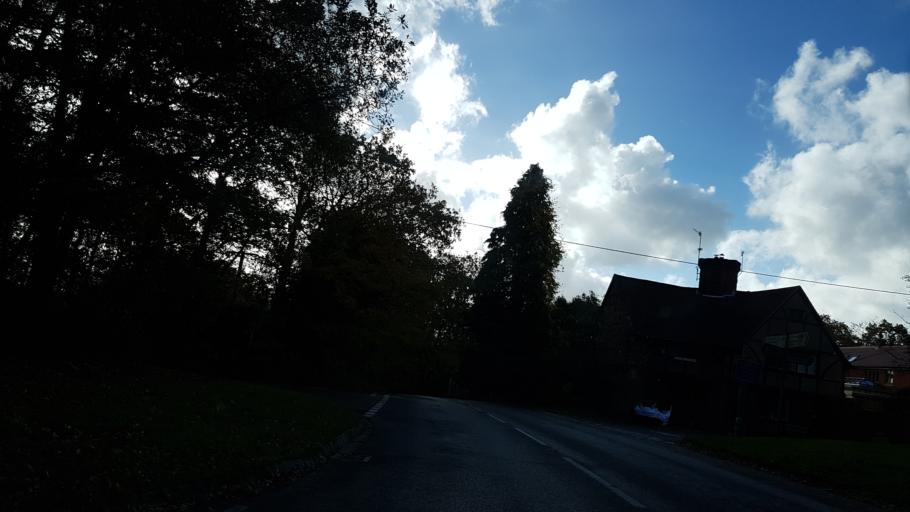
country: GB
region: England
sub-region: Surrey
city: Milford
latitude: 51.1325
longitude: -0.6729
